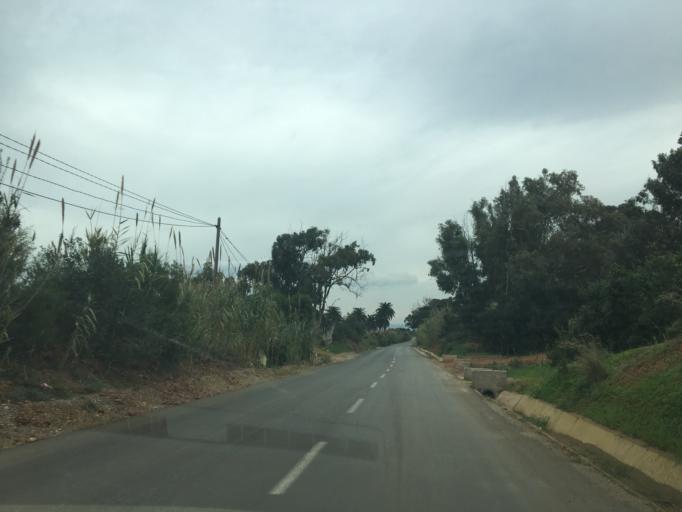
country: DZ
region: Tipaza
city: Tipasa
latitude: 36.6386
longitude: 2.3807
